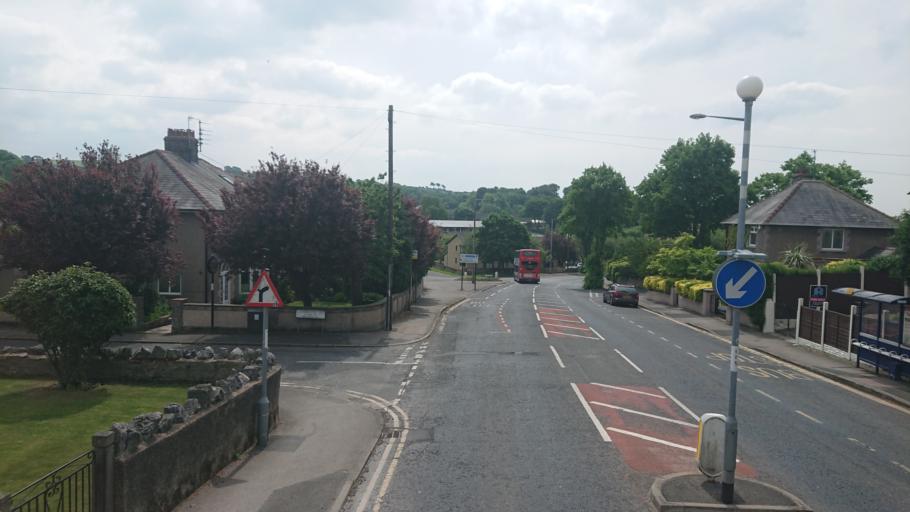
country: GB
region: England
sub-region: Lancashire
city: Lancaster
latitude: 54.0353
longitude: -2.7876
